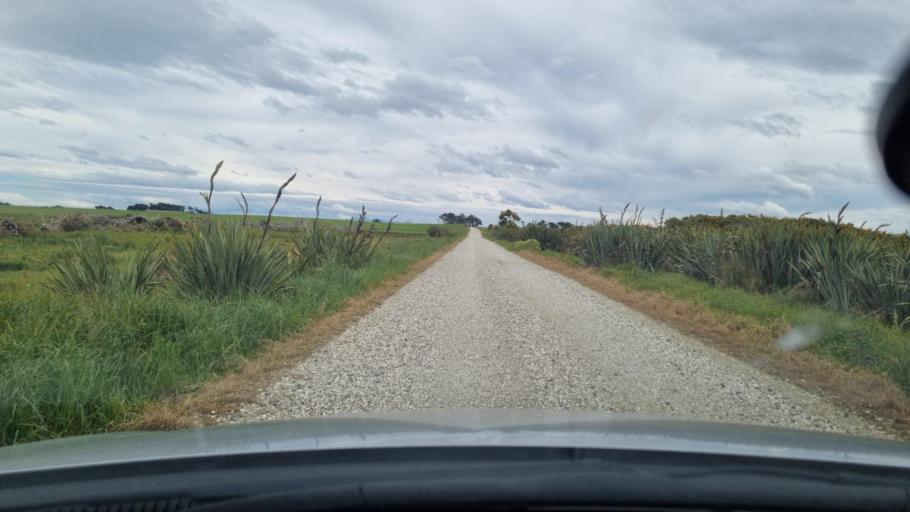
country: NZ
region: Southland
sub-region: Invercargill City
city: Invercargill
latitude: -46.3962
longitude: 168.2681
